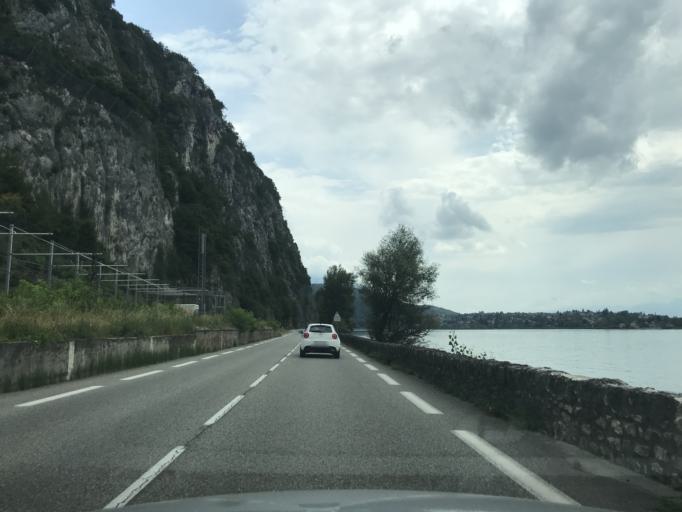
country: FR
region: Rhone-Alpes
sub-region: Departement de la Savoie
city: Brison-Saint-Innocent
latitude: 45.7497
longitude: 5.8823
